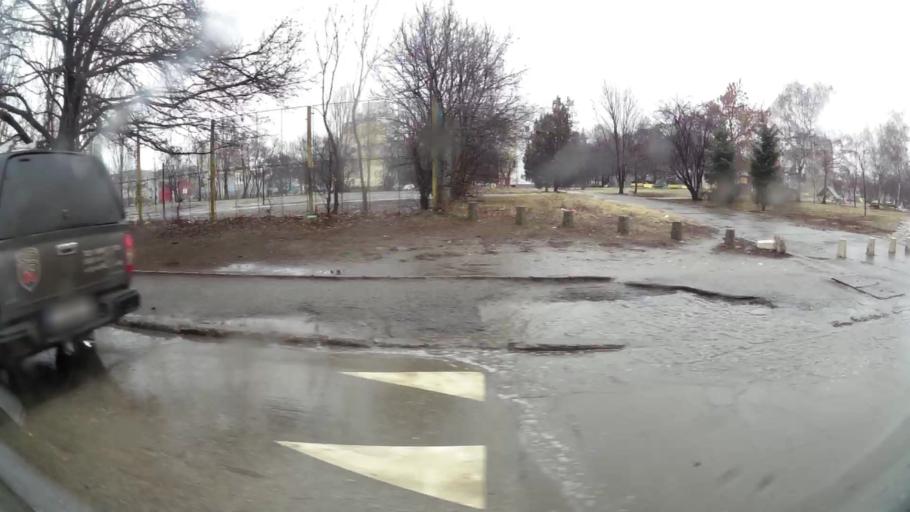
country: BG
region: Sofia-Capital
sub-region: Stolichna Obshtina
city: Sofia
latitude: 42.6666
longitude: 23.3974
